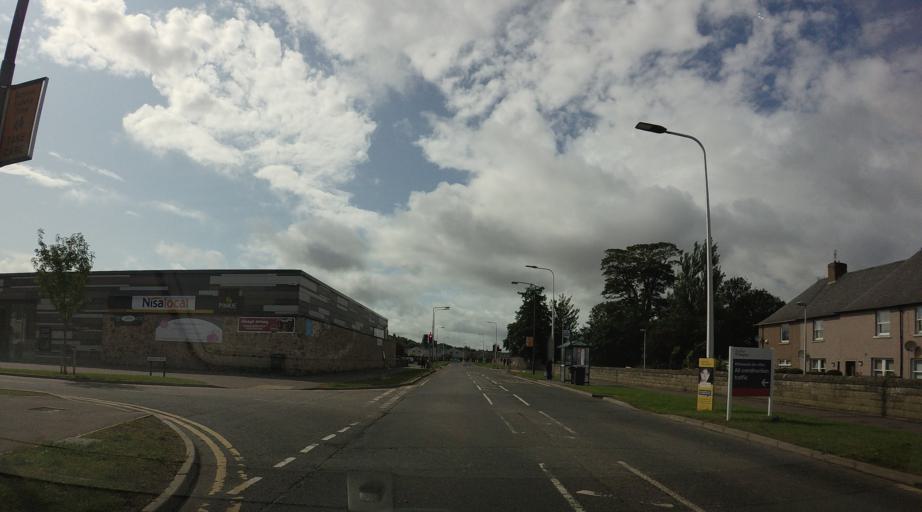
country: GB
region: Scotland
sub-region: East Lothian
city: Musselburgh
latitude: 55.9419
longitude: -3.0336
